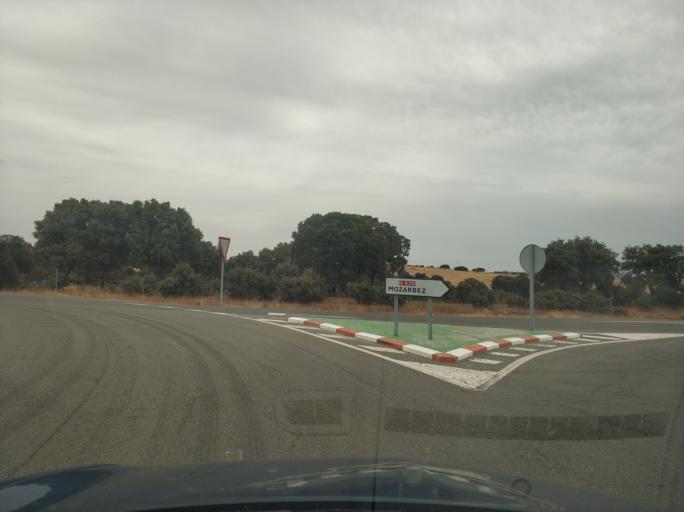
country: ES
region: Castille and Leon
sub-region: Provincia de Salamanca
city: Mozarbez
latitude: 40.8678
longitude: -5.6549
